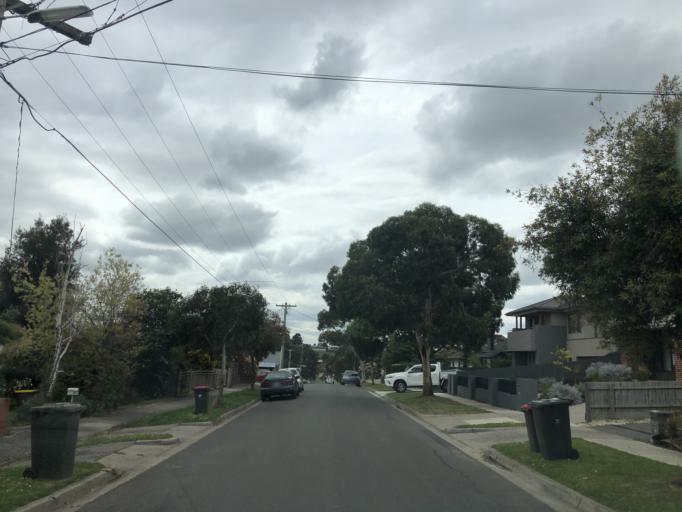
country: AU
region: Victoria
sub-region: Monash
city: Ashwood
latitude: -37.8692
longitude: 145.1053
